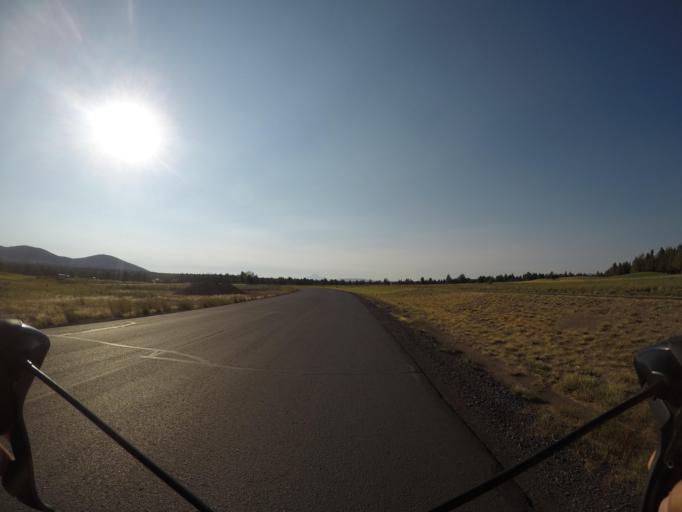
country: US
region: Oregon
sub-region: Deschutes County
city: Redmond
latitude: 44.2615
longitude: -121.2517
